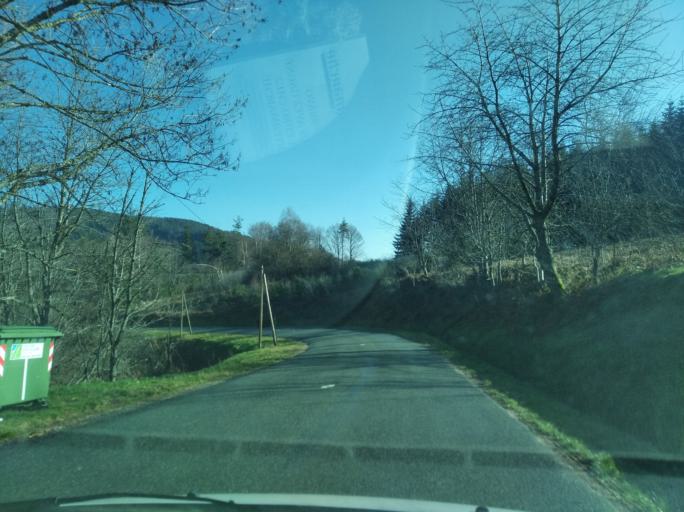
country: FR
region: Auvergne
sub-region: Departement de l'Allier
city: Le Mayet-de-Montagne
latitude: 46.1063
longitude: 3.7691
